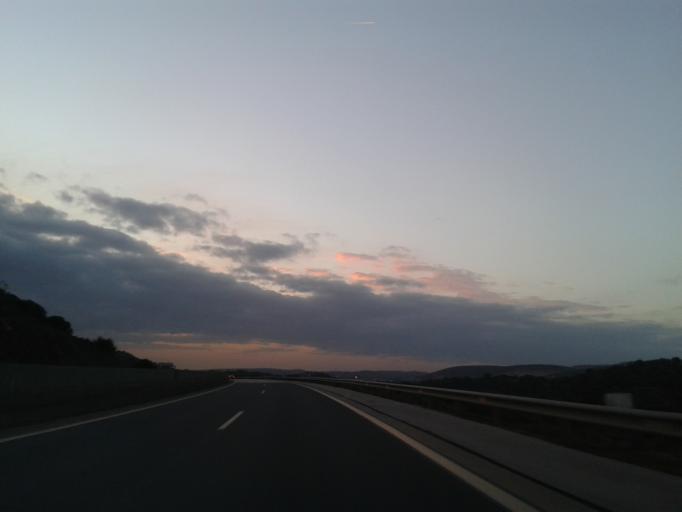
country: PT
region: Faro
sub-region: Loule
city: Loule
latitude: 37.1241
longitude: -8.0687
